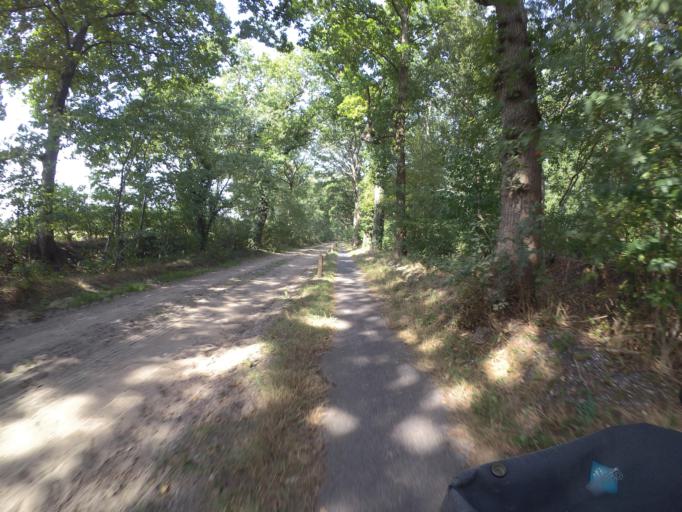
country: NL
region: Drenthe
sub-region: Gemeente Westerveld
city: Havelte
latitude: 52.7633
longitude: 6.2175
